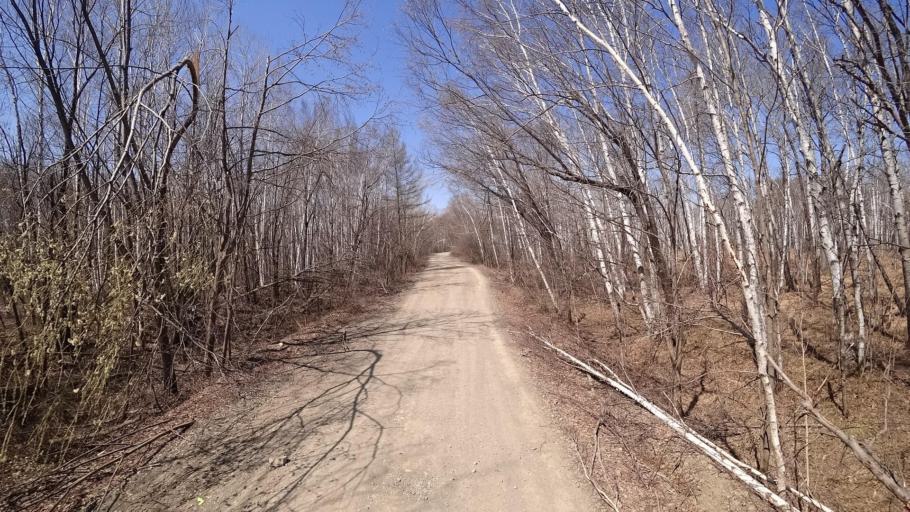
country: RU
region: Khabarovsk Krai
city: Khurba
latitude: 50.4177
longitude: 136.8363
